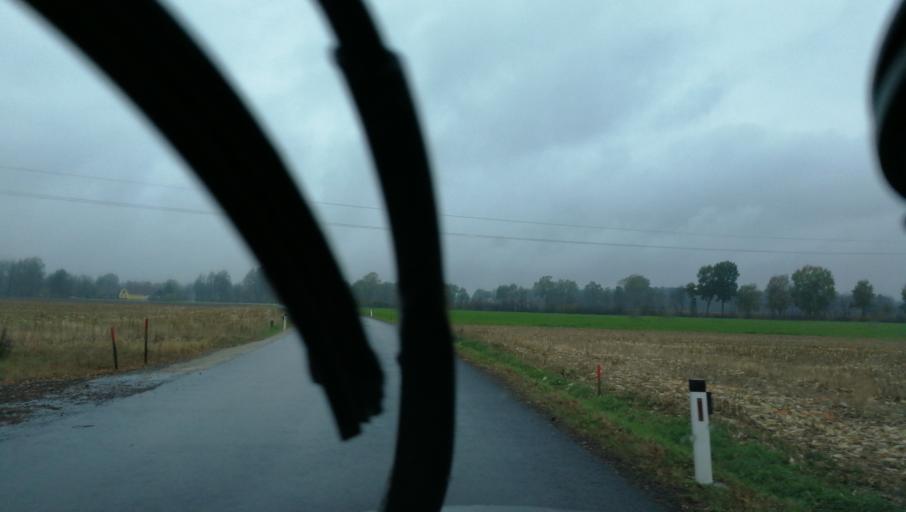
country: AT
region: Styria
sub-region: Politischer Bezirk Suedoststeiermark
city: Weinburg am Sassbach
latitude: 46.7329
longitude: 15.6844
